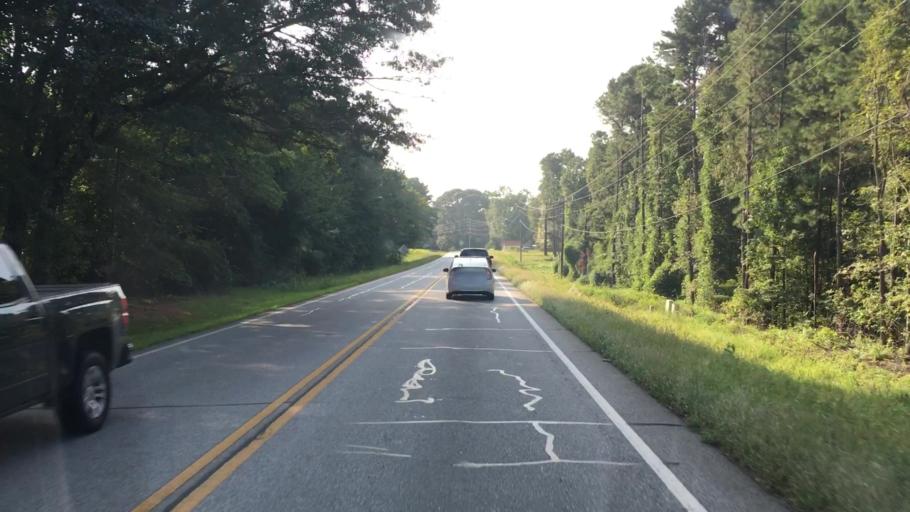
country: US
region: Georgia
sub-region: Jackson County
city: Braselton
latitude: 34.1334
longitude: -83.7694
